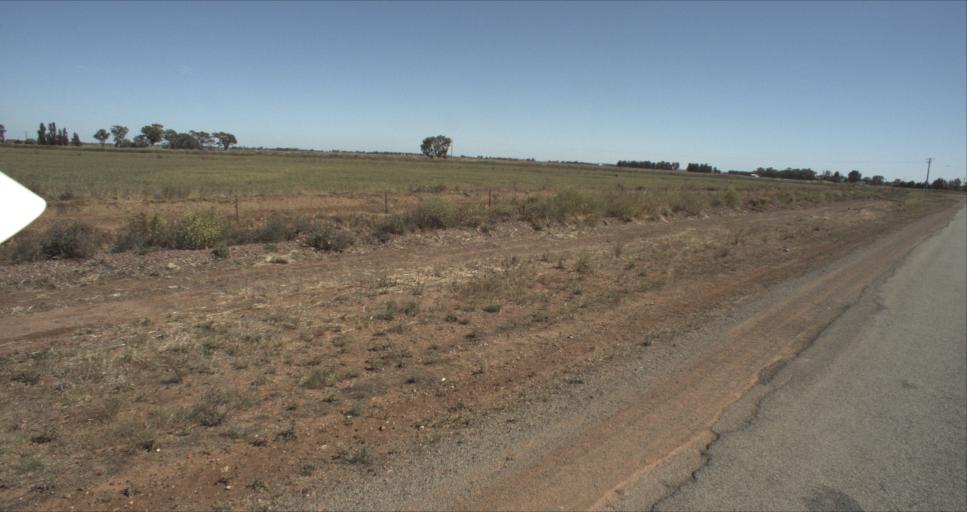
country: AU
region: New South Wales
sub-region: Leeton
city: Leeton
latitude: -34.5522
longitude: 146.3144
